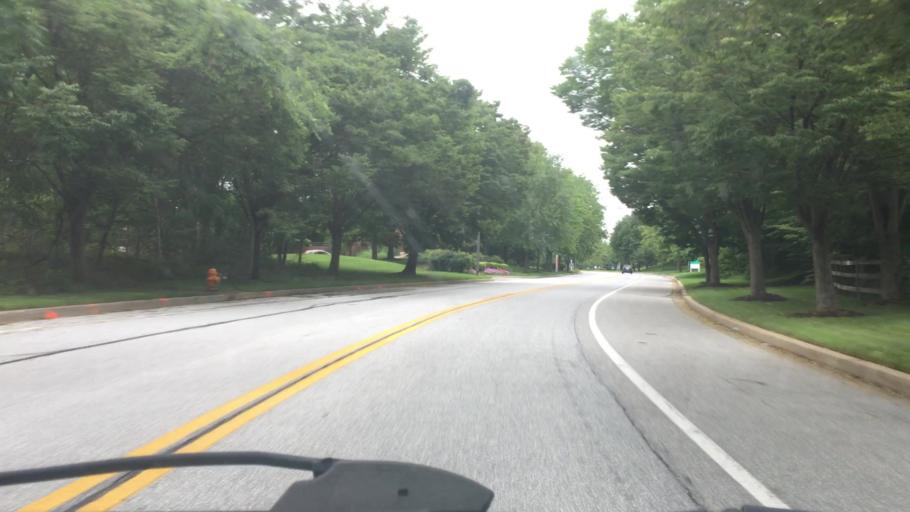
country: US
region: Maryland
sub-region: Howard County
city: Savage
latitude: 39.1668
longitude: -76.8421
